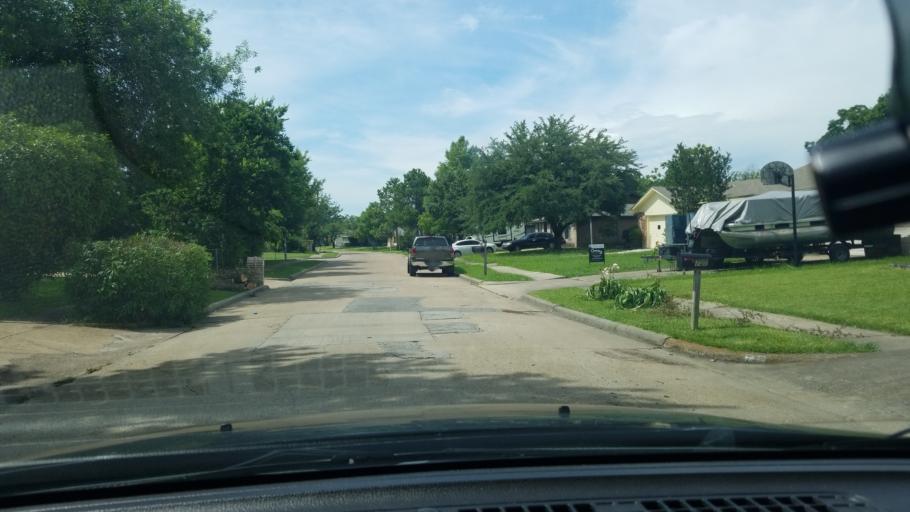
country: US
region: Texas
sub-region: Dallas County
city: Mesquite
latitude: 32.7582
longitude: -96.5792
